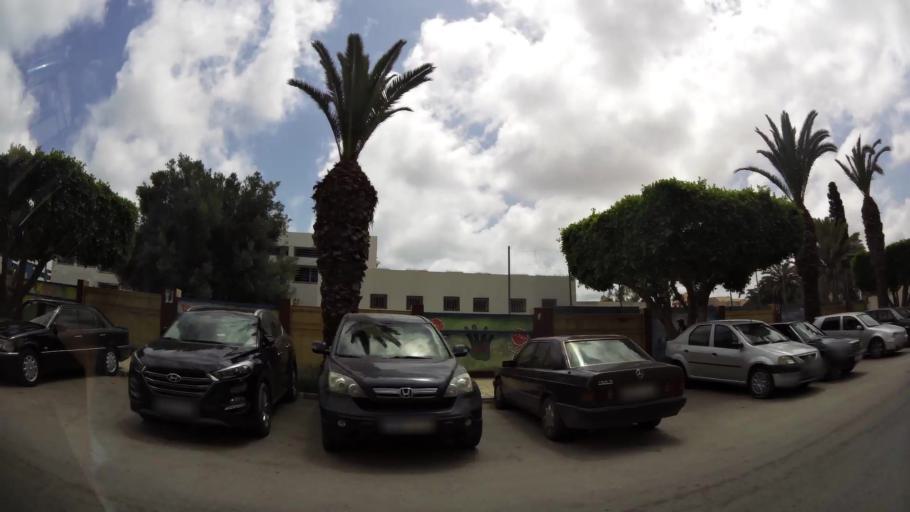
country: MA
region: Oriental
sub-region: Nador
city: Nador
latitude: 35.1715
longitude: -2.9245
